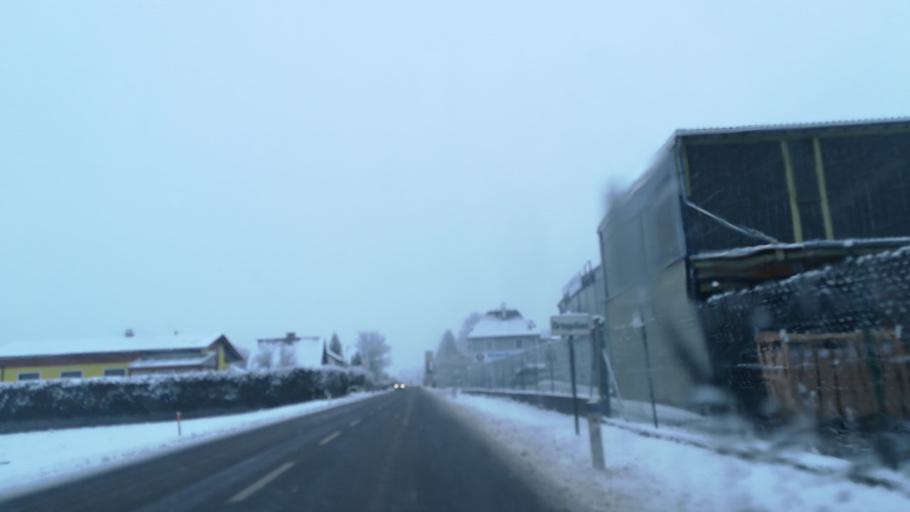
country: AT
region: Styria
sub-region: Politischer Bezirk Murtal
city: Knittelfeld
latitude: 47.2184
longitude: 14.8138
